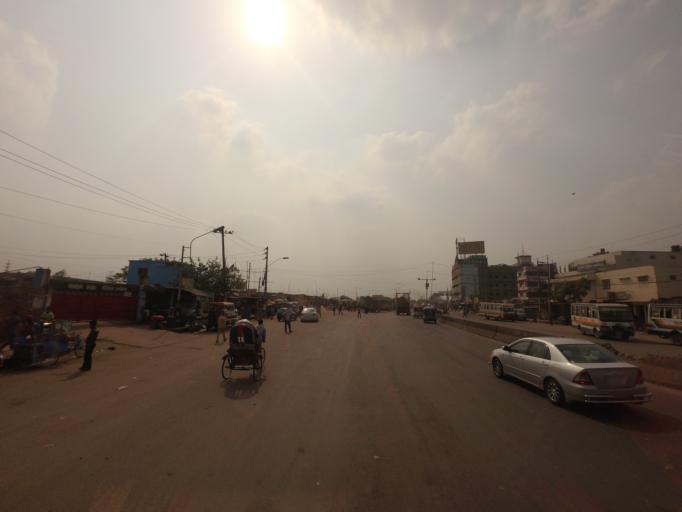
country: BD
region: Dhaka
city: Azimpur
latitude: 23.7829
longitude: 90.3400
